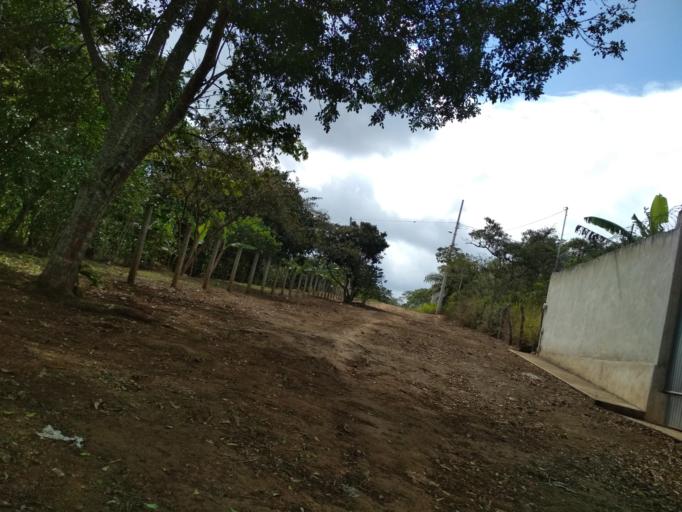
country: MX
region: Veracruz
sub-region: Emiliano Zapata
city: Jacarandas
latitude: 19.4972
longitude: -96.8350
